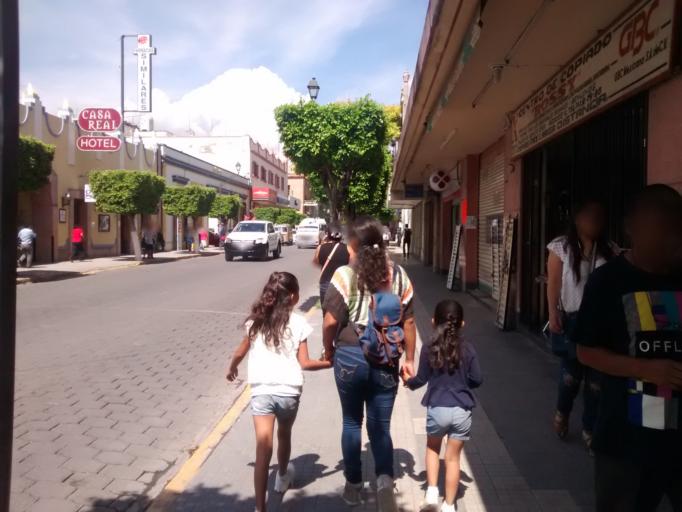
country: MX
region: Puebla
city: Tehuacan
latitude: 18.4610
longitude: -97.3941
